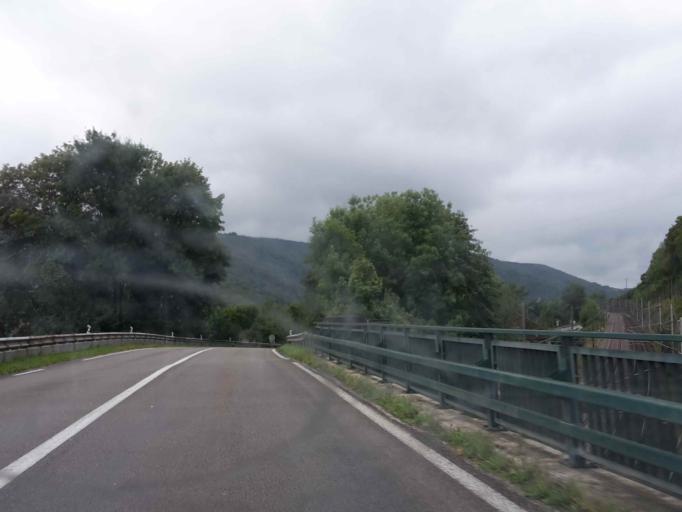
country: FR
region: Franche-Comte
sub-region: Departement du Doubs
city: Novillars
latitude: 47.2829
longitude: 6.1296
